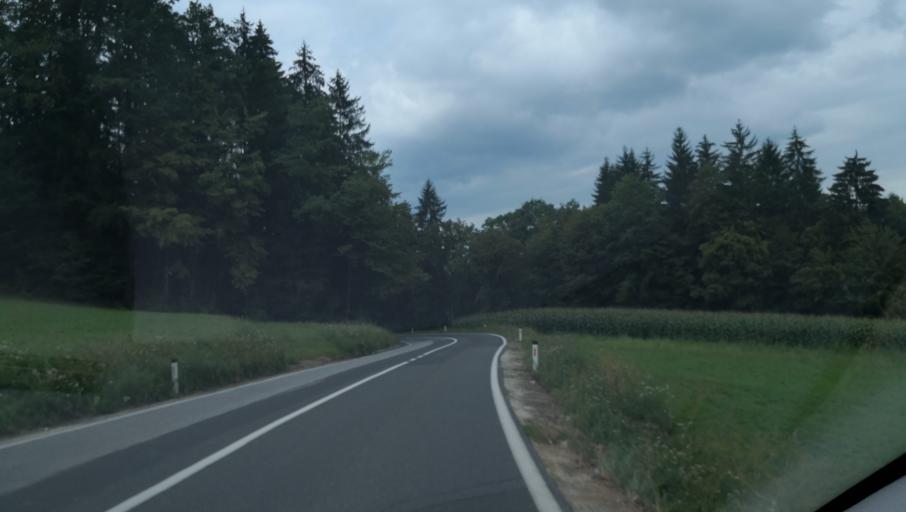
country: SI
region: Novo Mesto
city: Novo Mesto
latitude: 45.7486
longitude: 15.2062
